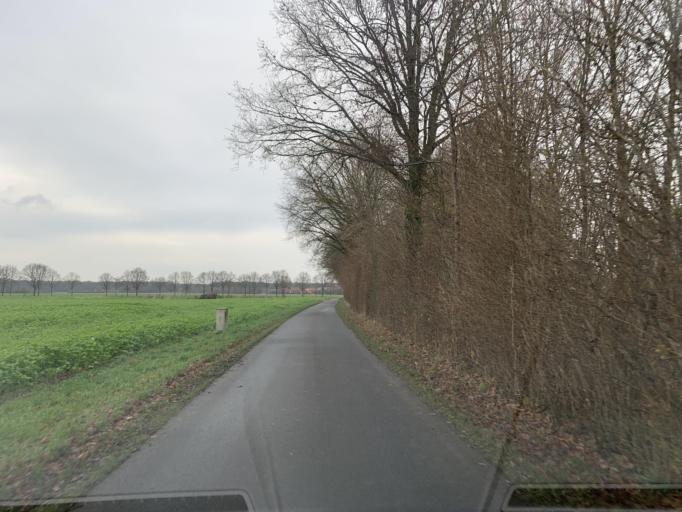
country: DE
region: North Rhine-Westphalia
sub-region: Regierungsbezirk Munster
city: Senden
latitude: 51.8881
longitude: 7.5582
